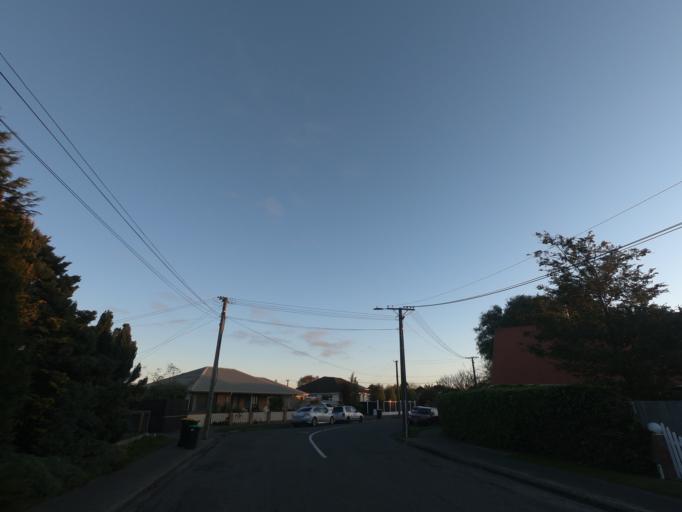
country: NZ
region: Canterbury
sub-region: Selwyn District
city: Prebbleton
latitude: -43.5758
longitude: 172.5604
